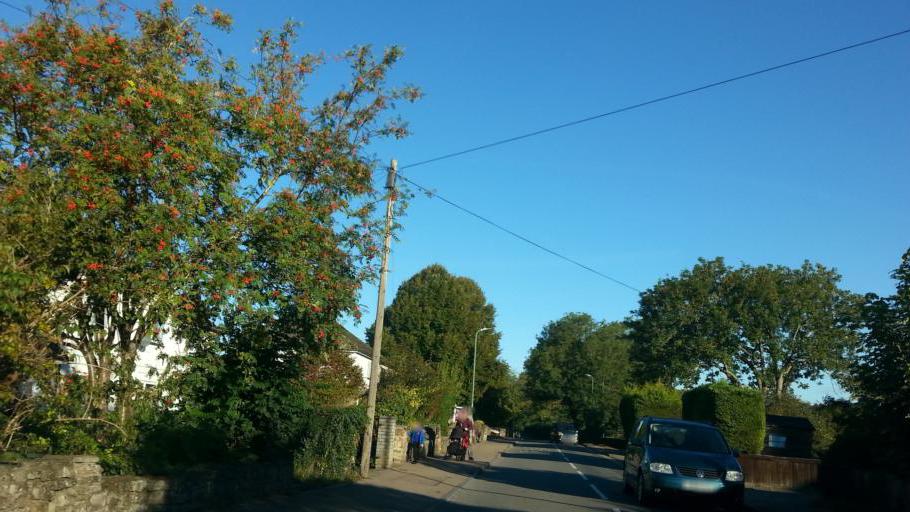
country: GB
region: Wales
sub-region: Monmouthshire
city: Monmouth
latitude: 51.8140
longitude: -2.7267
